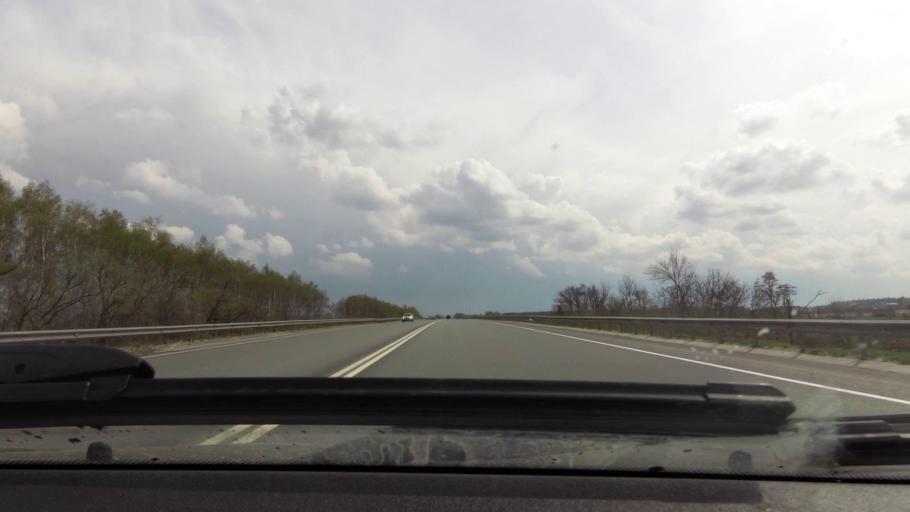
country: RU
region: Rjazan
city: Bagramovo
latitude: 54.7373
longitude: 39.4502
